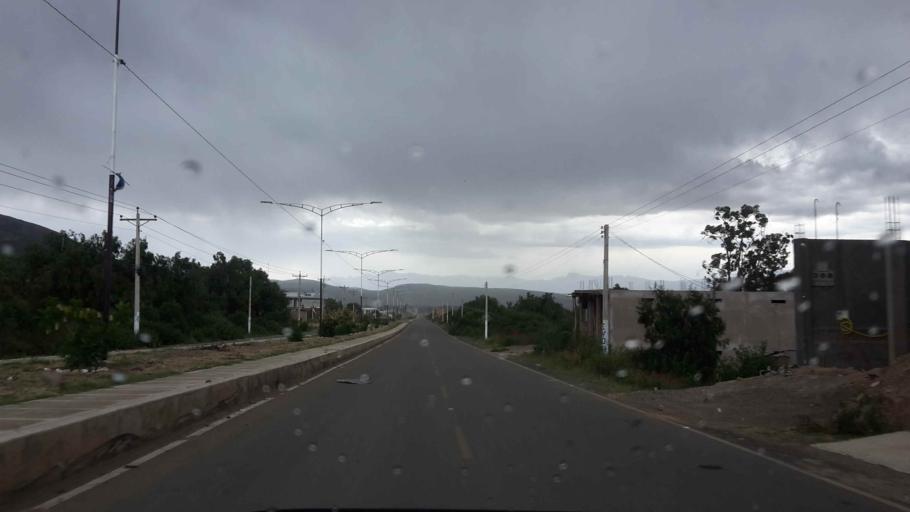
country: BO
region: Cochabamba
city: Tarata
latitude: -17.6044
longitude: -66.0314
